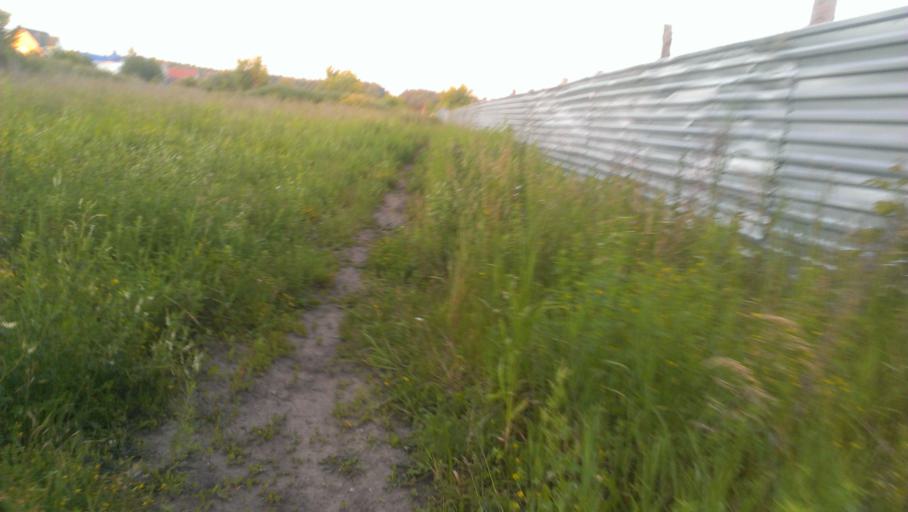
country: RU
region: Altai Krai
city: Novosilikatnyy
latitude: 53.3640
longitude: 83.6500
